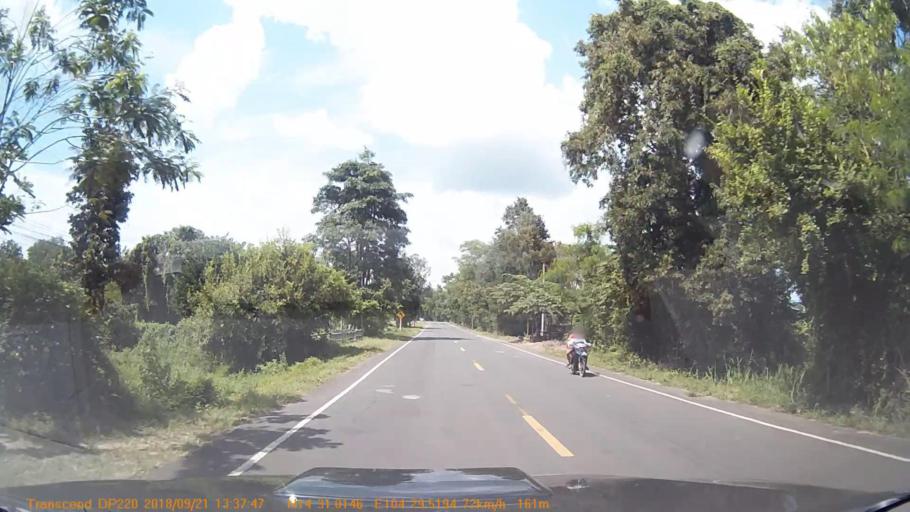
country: TH
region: Sisaket
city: Khun Han
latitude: 14.5170
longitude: 104.4920
